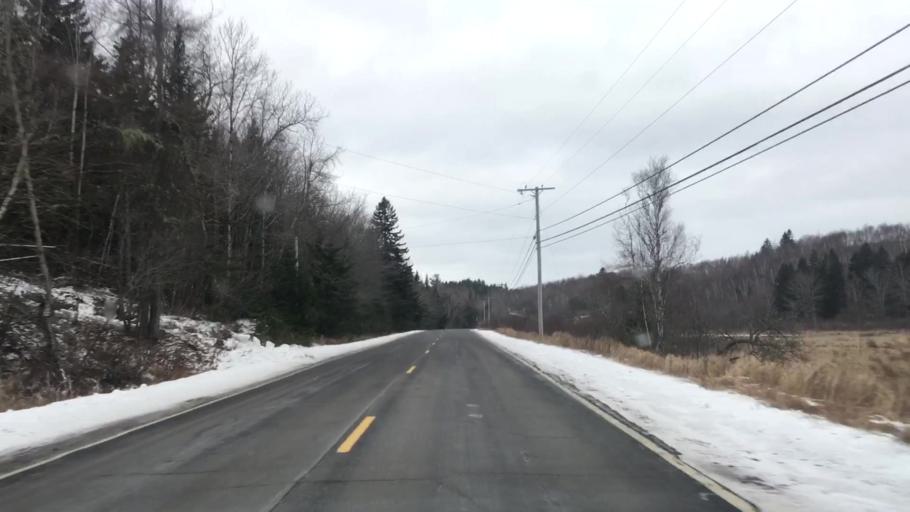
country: US
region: Maine
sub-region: Washington County
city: Machiasport
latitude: 44.7101
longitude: -67.3698
